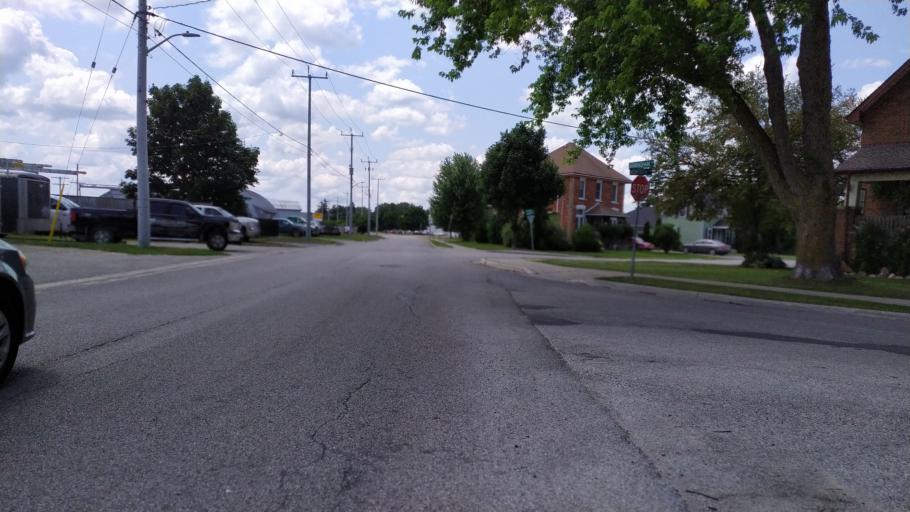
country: CA
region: Ontario
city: Stratford
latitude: 43.3610
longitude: -80.9944
